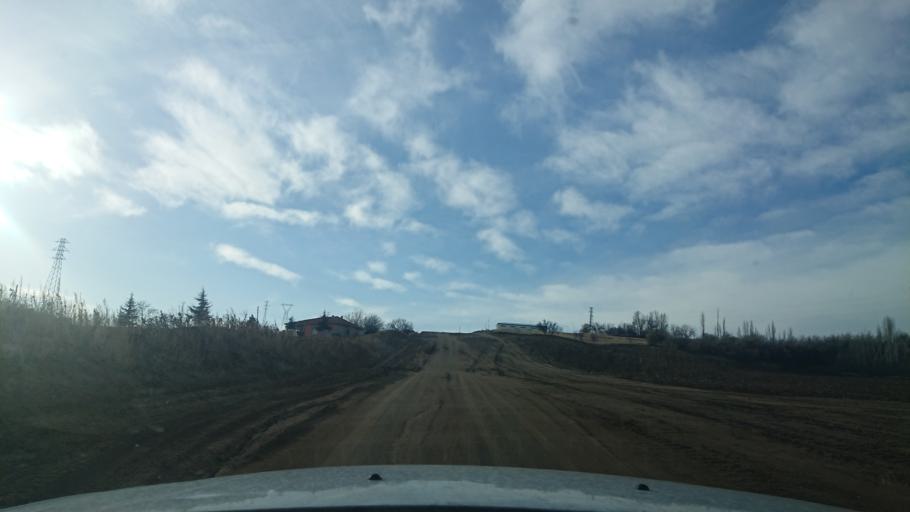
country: TR
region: Aksaray
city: Agacoren
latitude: 38.8566
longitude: 33.9429
